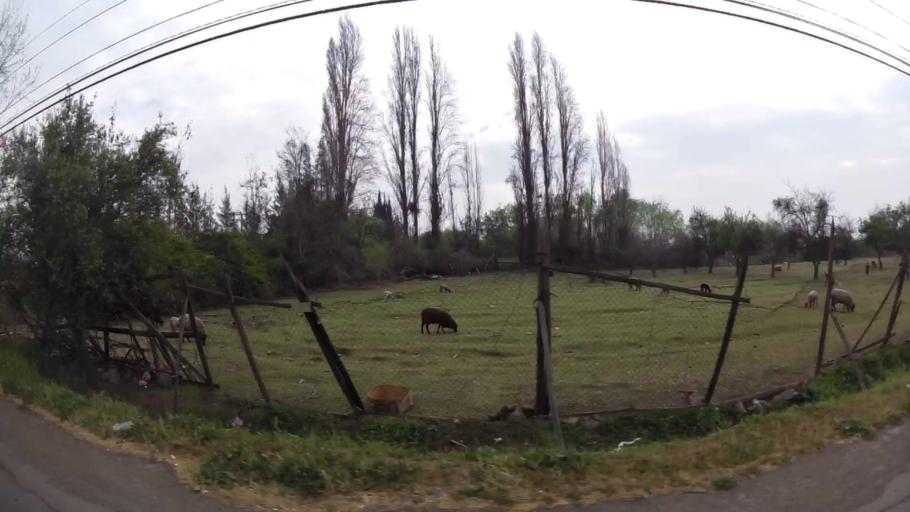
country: CL
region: Santiago Metropolitan
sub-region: Provincia de Chacabuco
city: Lampa
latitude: -33.2268
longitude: -70.7782
